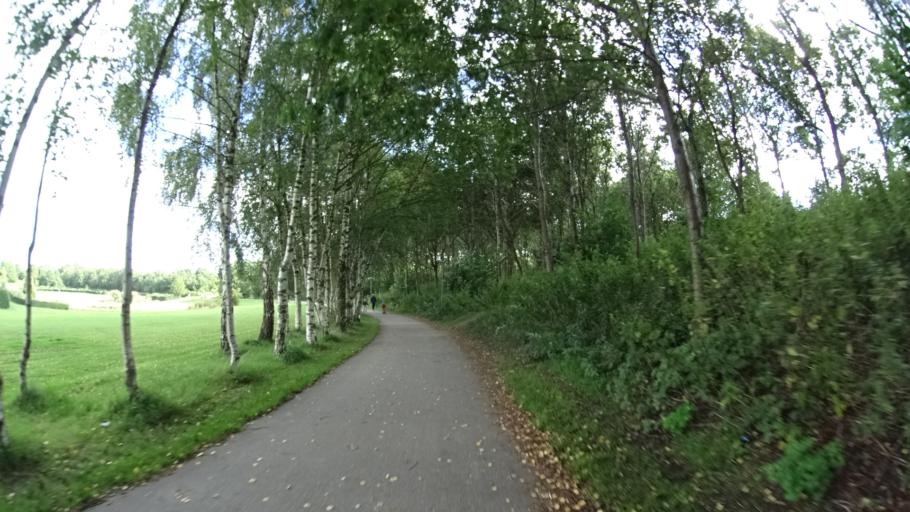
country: DK
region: Central Jutland
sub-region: Arhus Kommune
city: Arhus
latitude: 56.1117
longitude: 10.1861
